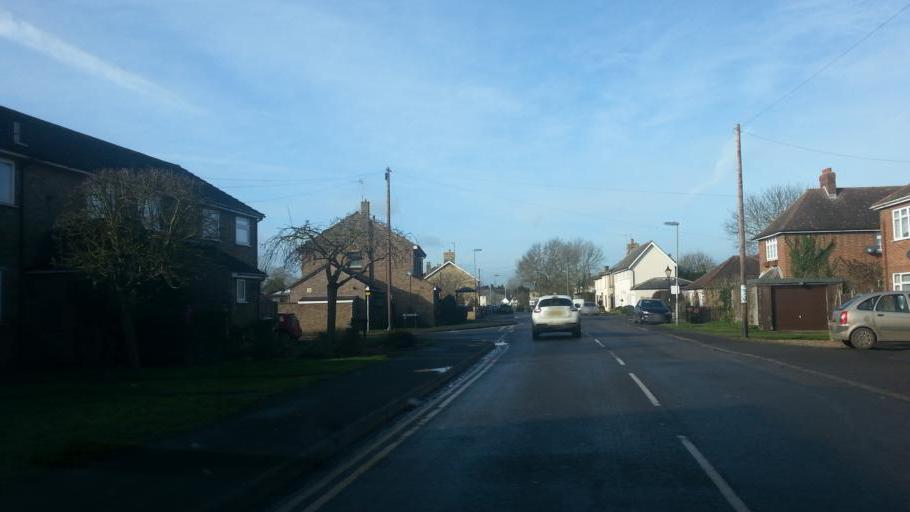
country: GB
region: England
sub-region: Cambridgeshire
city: Warboys
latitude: 52.4035
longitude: -0.0733
